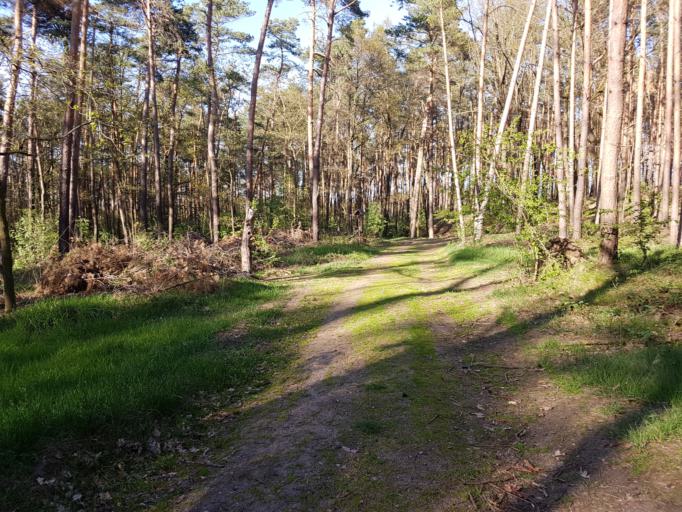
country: DE
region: Brandenburg
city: Groden
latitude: 51.3989
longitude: 13.5728
